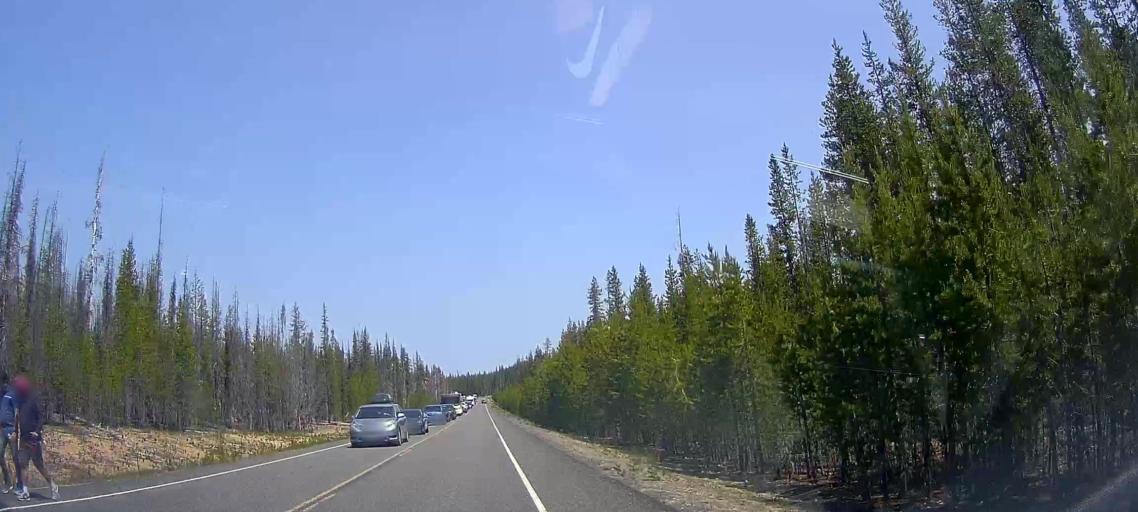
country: US
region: Oregon
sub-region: Lane County
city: Oakridge
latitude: 43.0826
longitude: -122.1170
